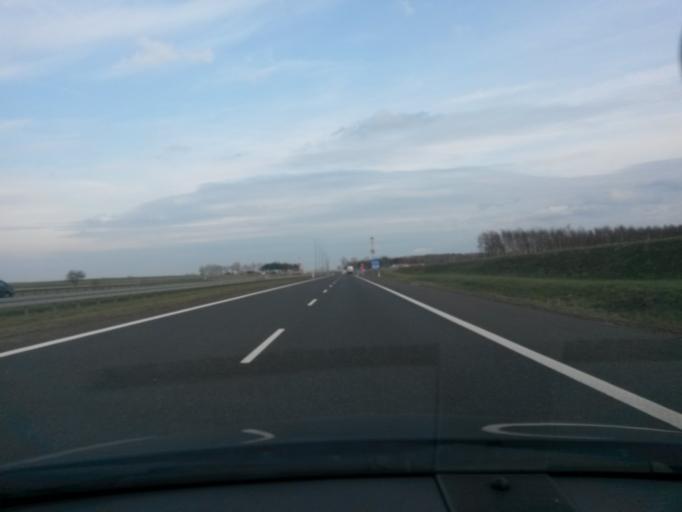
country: PL
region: Lodz Voivodeship
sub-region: Powiat zgierski
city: Parzeczew
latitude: 51.9474
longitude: 19.1694
